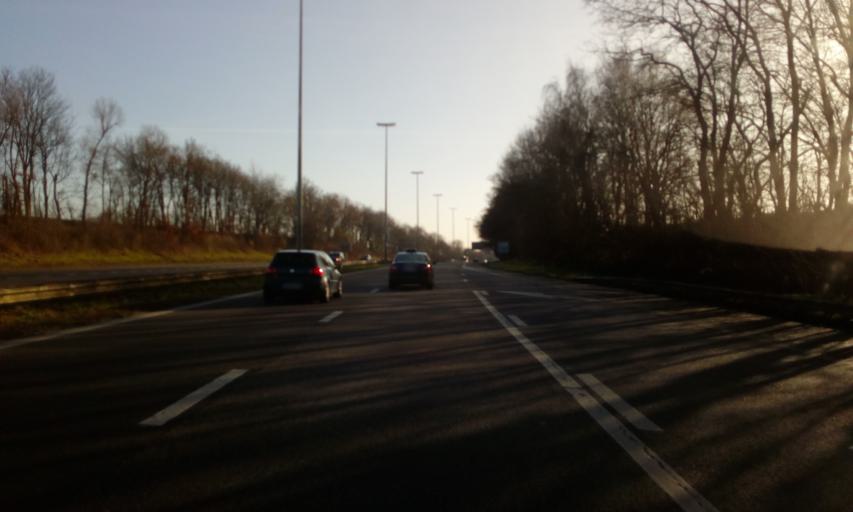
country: BE
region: Wallonia
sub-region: Province du Hainaut
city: Brunehault
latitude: 50.5108
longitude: 4.4135
